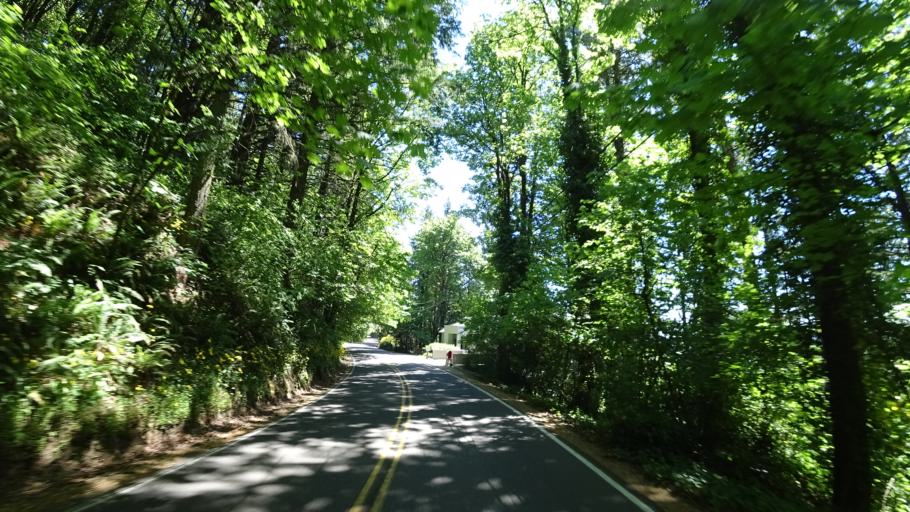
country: US
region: Oregon
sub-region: Multnomah County
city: Portland
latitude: 45.4976
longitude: -122.7103
